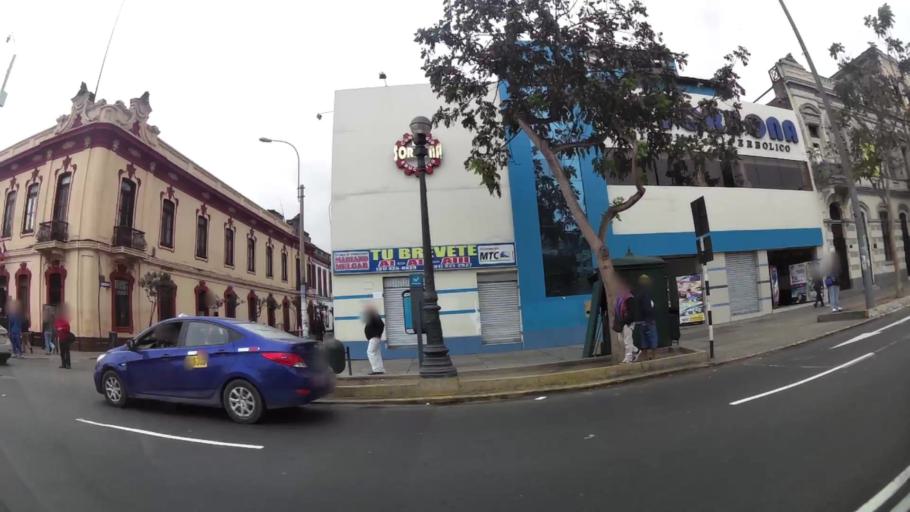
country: PE
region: Lima
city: Lima
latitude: -12.0599
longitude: -77.0404
